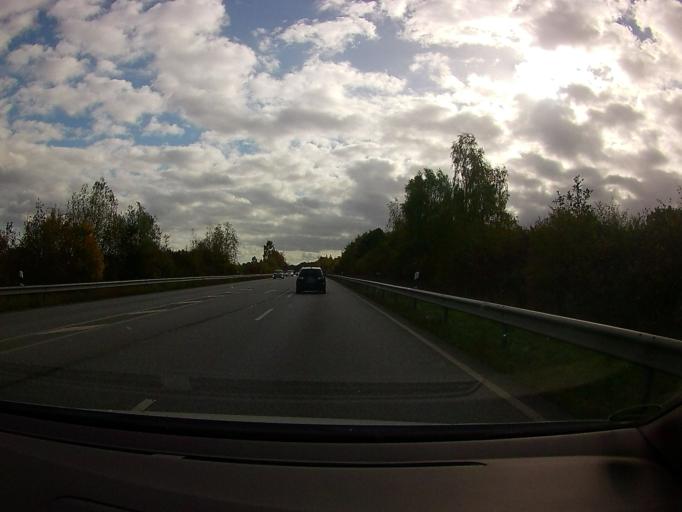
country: DE
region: Schleswig-Holstein
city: Kuddeworde
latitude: 53.5761
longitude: 10.3995
